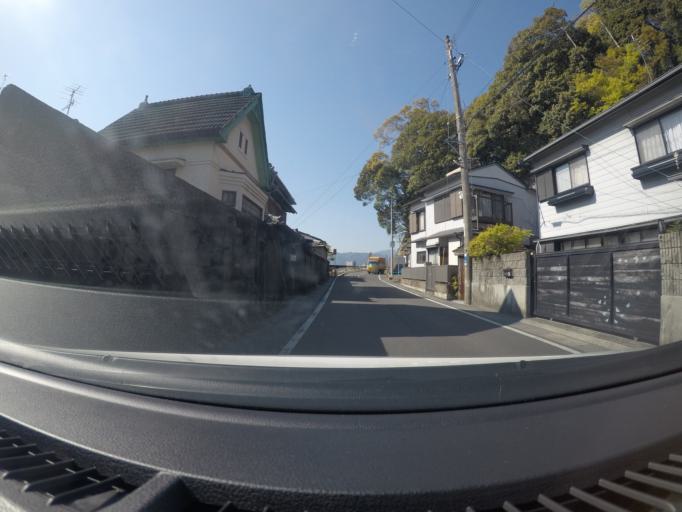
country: JP
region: Kochi
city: Kochi-shi
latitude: 33.5444
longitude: 133.5702
